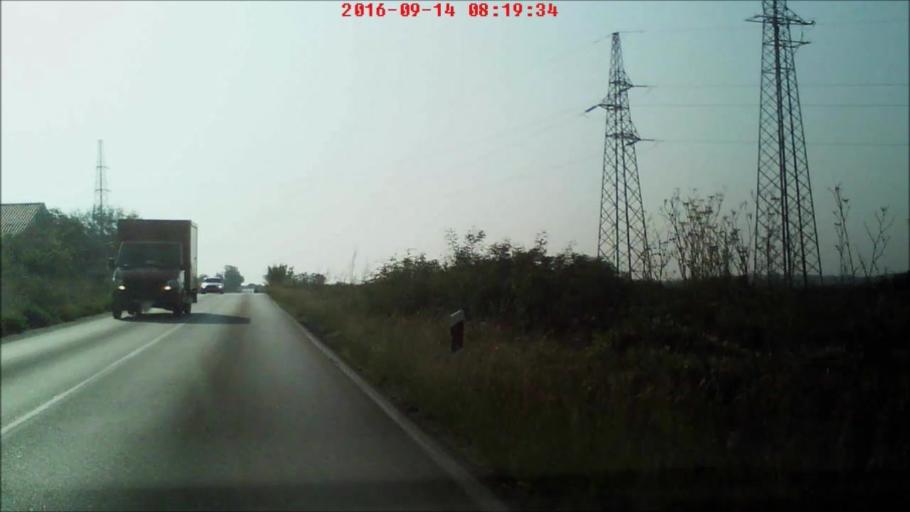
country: HR
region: Zadarska
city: Nin
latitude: 44.2317
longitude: 15.1915
